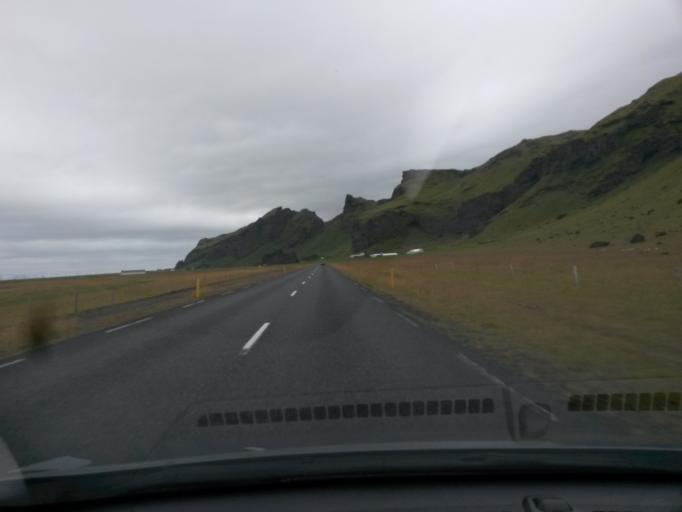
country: IS
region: South
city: Vestmannaeyjar
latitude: 63.5224
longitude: -19.5325
